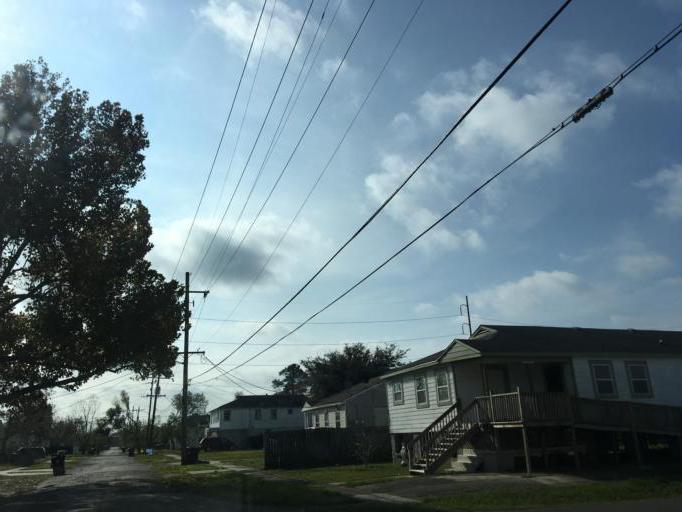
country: US
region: Louisiana
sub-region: Orleans Parish
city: New Orleans
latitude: 29.9901
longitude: -90.0550
